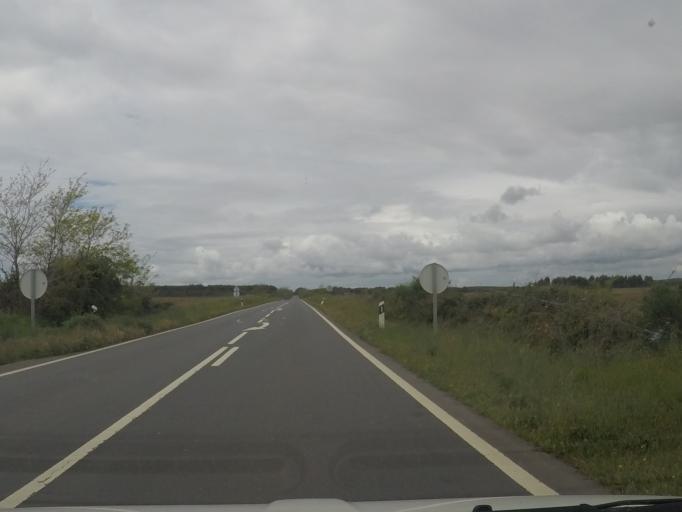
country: PT
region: Setubal
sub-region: Santiago do Cacem
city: Cercal
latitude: 37.8405
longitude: -8.7037
